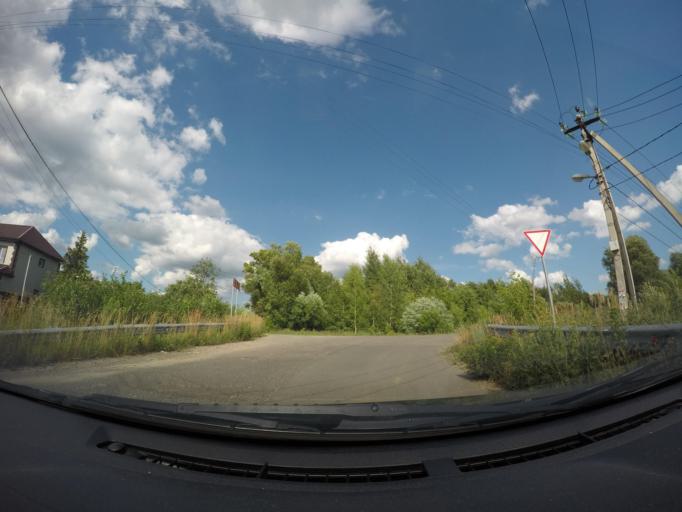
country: RU
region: Moskovskaya
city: Rechitsy
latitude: 55.6077
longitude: 38.5244
